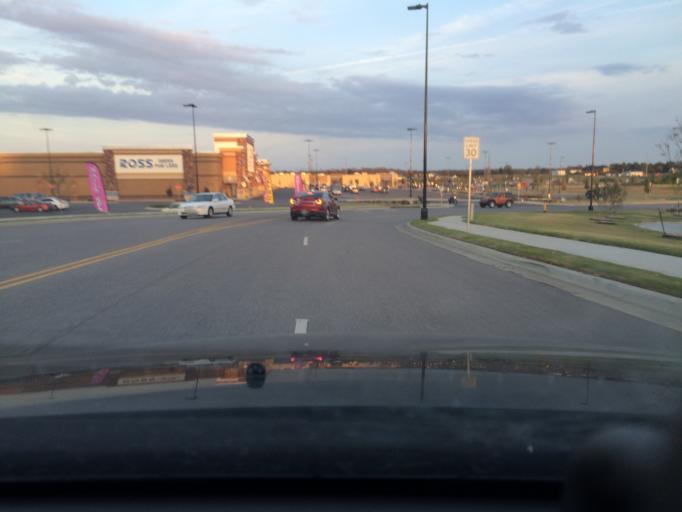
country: US
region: Oklahoma
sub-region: Rogers County
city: Catoosa
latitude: 36.1655
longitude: -95.7611
